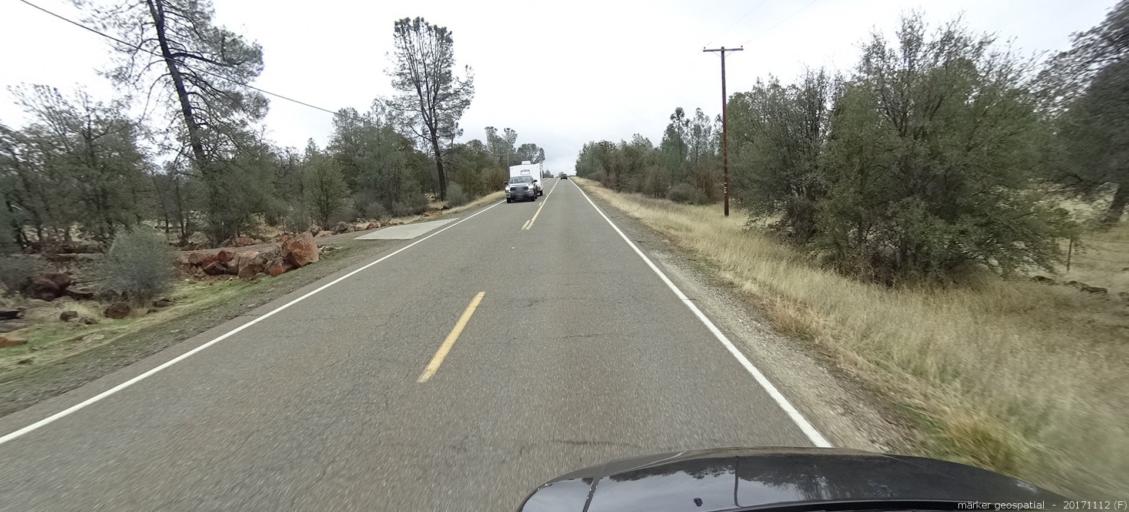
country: US
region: California
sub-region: Shasta County
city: Palo Cedro
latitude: 40.4854
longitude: -122.1156
